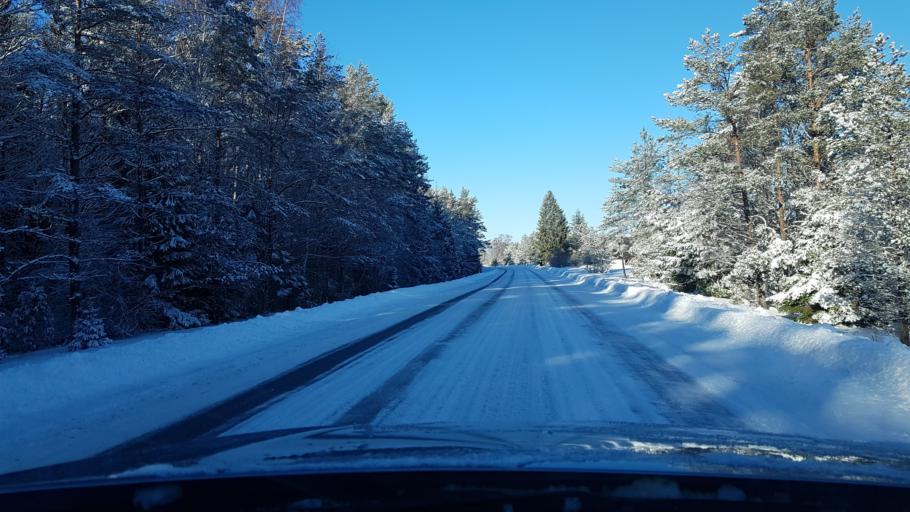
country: EE
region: Hiiumaa
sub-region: Kaerdla linn
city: Kardla
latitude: 58.9397
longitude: 22.7770
